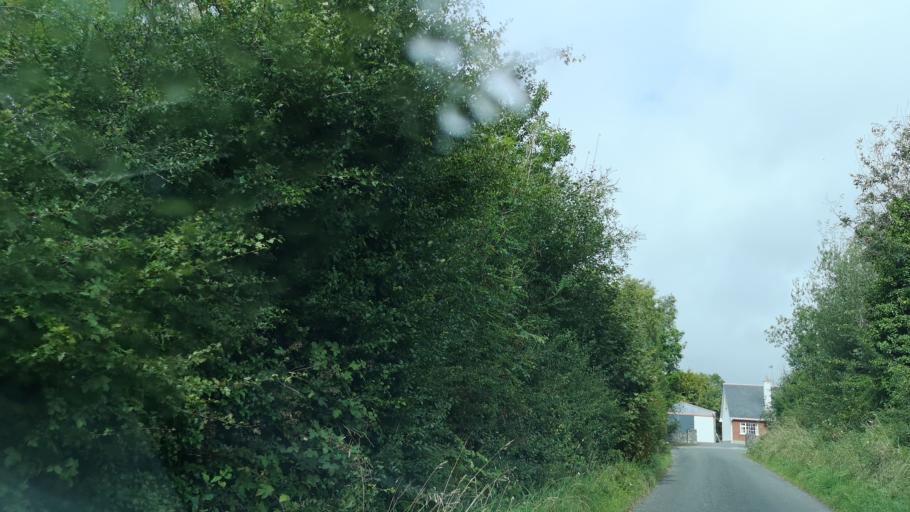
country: IE
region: Connaught
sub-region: County Galway
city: Loughrea
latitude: 53.3053
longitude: -8.6044
